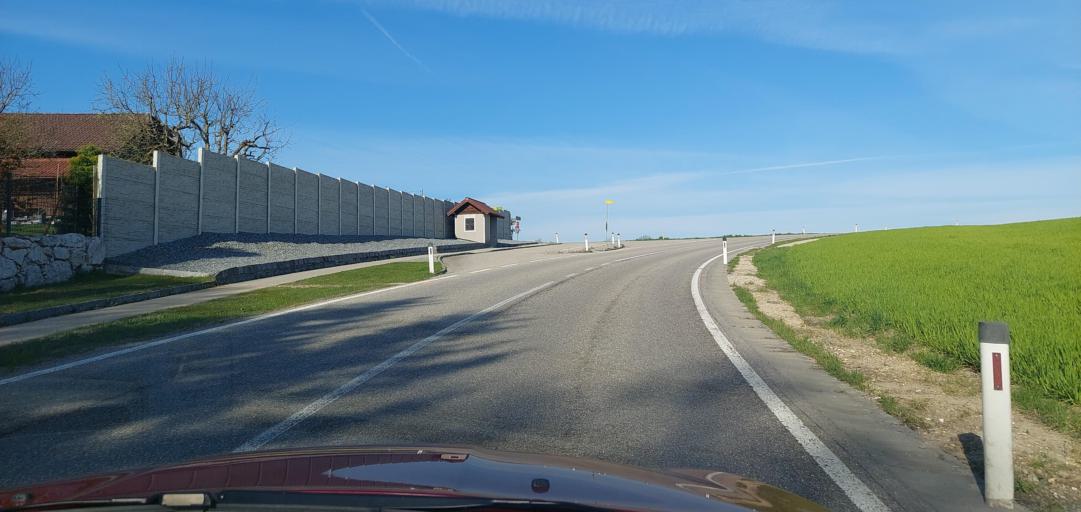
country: AT
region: Upper Austria
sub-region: Politischer Bezirk Ried im Innkreis
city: Ried im Innkreis
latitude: 48.1625
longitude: 13.5569
